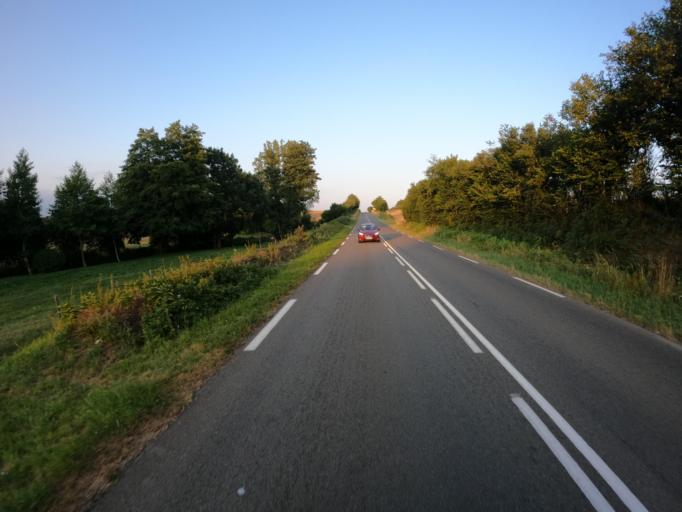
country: FR
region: Pays de la Loire
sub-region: Departement de la Mayenne
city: Meslay-du-Maine
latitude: 47.8719
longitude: -0.4930
